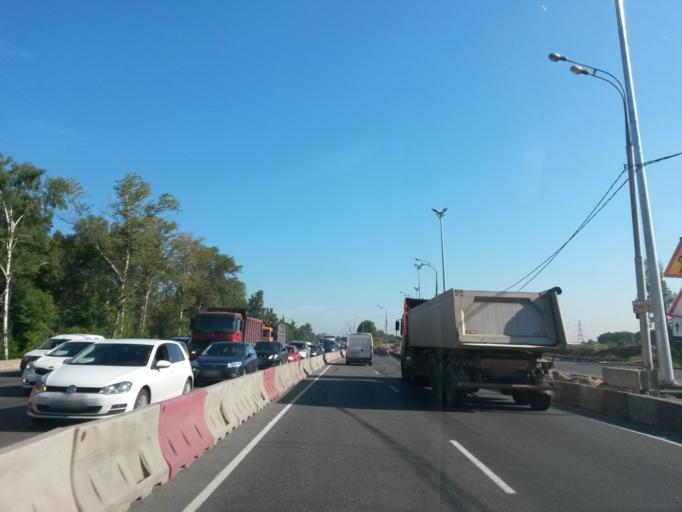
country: RU
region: Moskovskaya
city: Bolshevo
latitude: 55.9447
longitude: 37.8137
